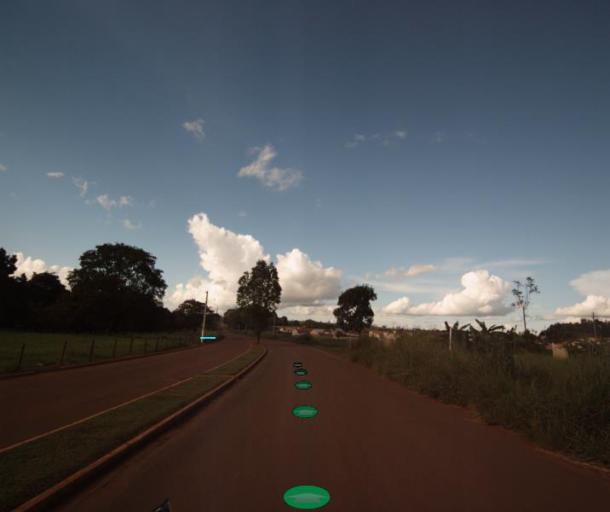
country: BR
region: Goias
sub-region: Itaberai
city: Itaberai
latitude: -16.0400
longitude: -49.7871
